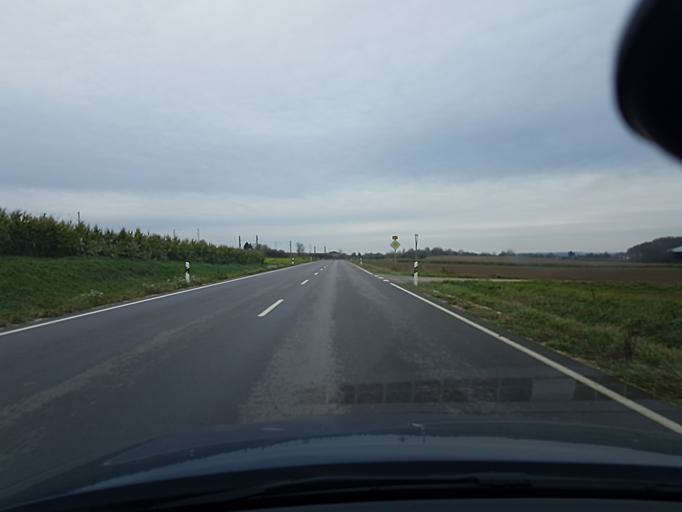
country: DE
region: Bavaria
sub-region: Upper Palatinate
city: Schierling
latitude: 48.8027
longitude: 12.1707
